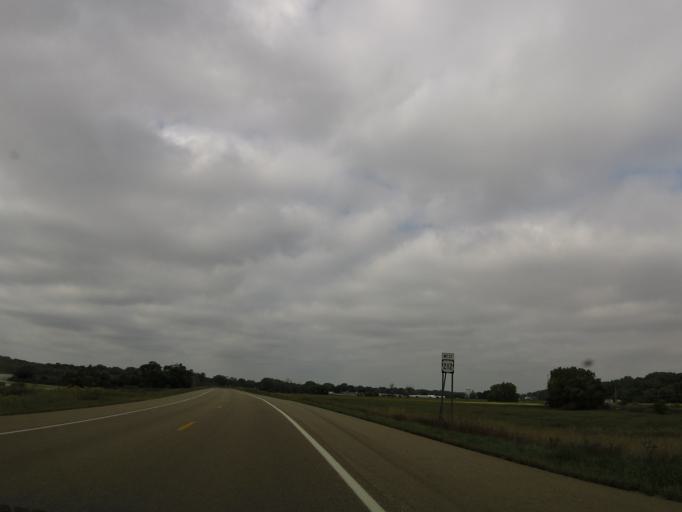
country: US
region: Minnesota
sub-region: Chippewa County
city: Montevideo
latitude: 44.9298
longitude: -95.7119
